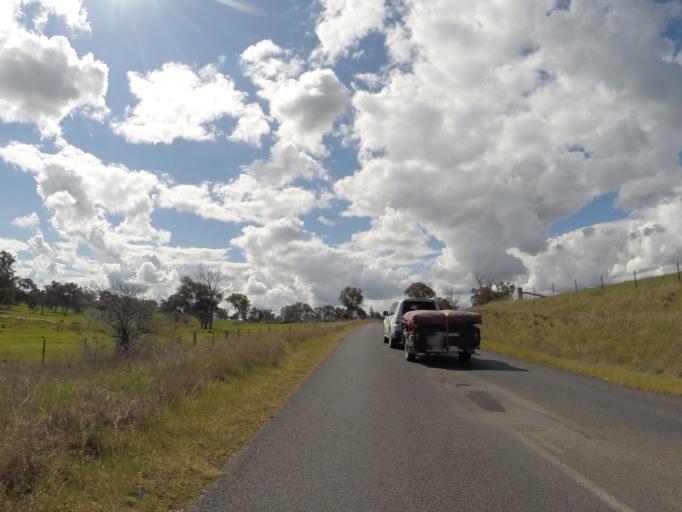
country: AU
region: New South Wales
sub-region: Yass Valley
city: Yass
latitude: -34.9401
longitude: 148.8724
